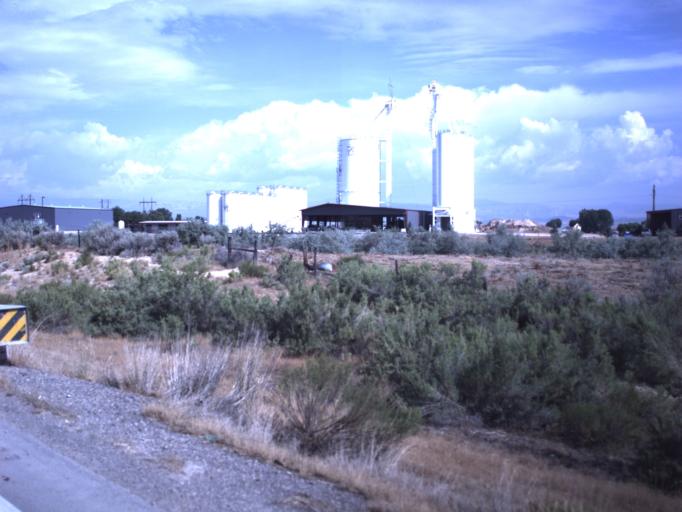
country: US
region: Utah
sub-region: Uintah County
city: Naples
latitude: 40.3983
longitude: -109.4618
